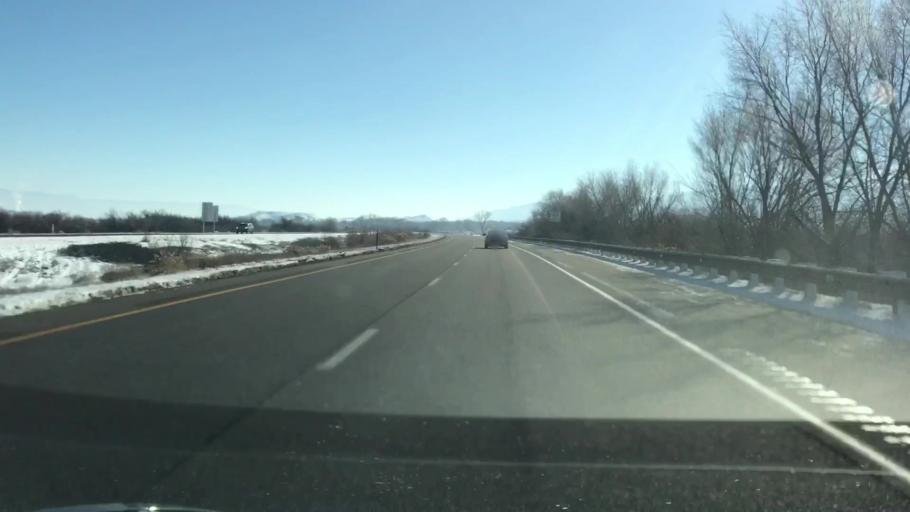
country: US
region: Colorado
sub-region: Mesa County
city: Loma
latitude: 39.1716
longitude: -108.7962
